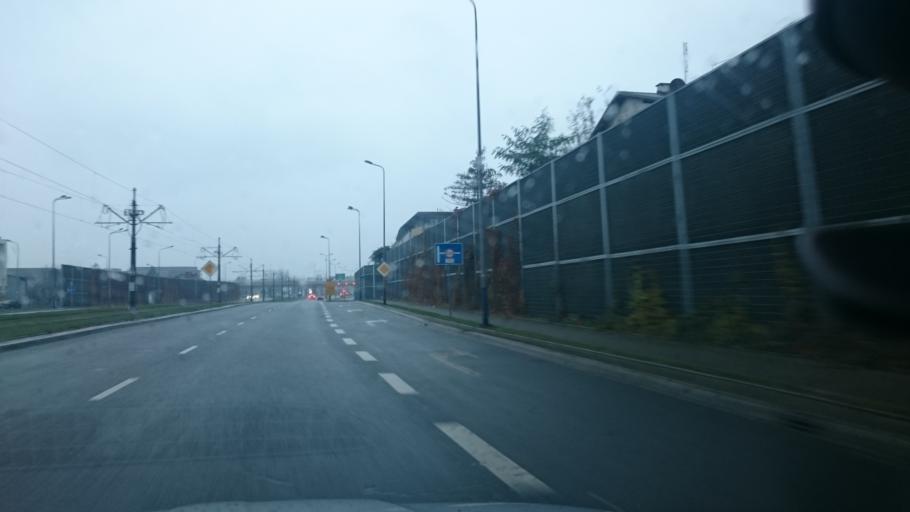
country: PL
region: Lesser Poland Voivodeship
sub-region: Krakow
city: Krakow
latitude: 50.0418
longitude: 19.9750
